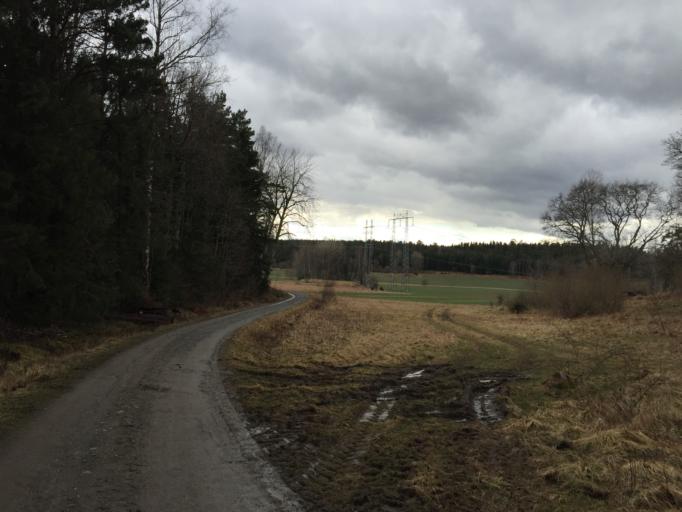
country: SE
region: Stockholm
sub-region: Salems Kommun
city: Ronninge
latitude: 59.2185
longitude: 17.7349
